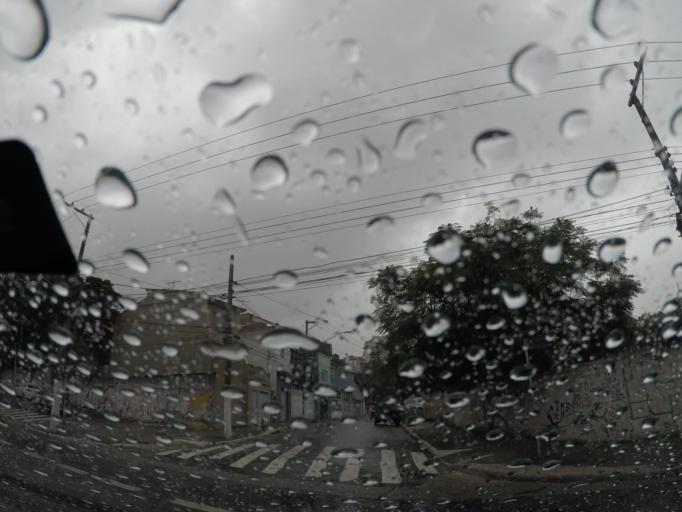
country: BR
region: Sao Paulo
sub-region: Diadema
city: Diadema
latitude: -23.6434
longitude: -46.6447
